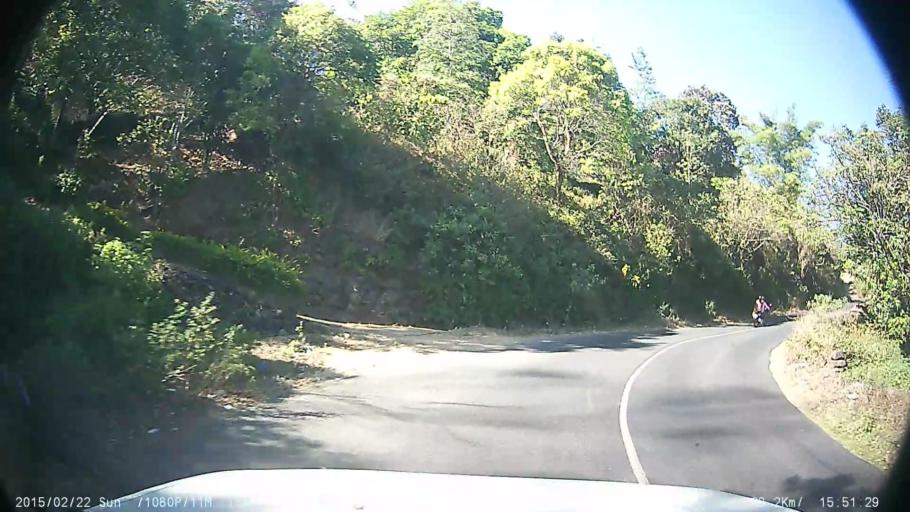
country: IN
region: Kerala
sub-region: Kottayam
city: Erattupetta
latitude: 9.5696
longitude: 77.0079
